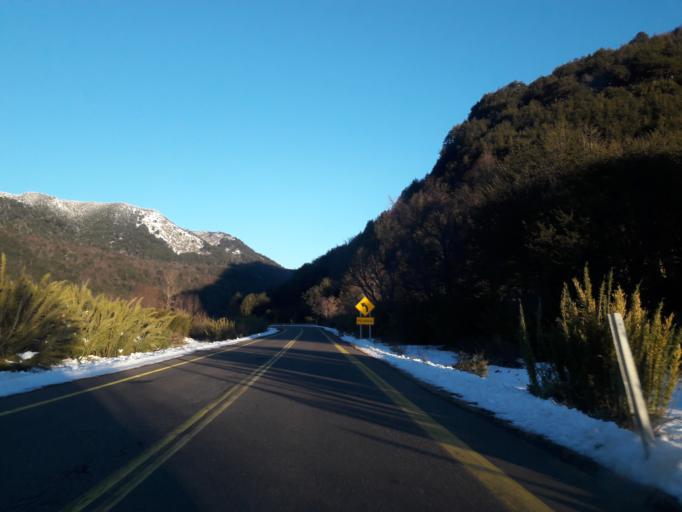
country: CL
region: Araucania
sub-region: Provincia de Cautin
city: Vilcun
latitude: -38.4873
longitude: -71.5288
